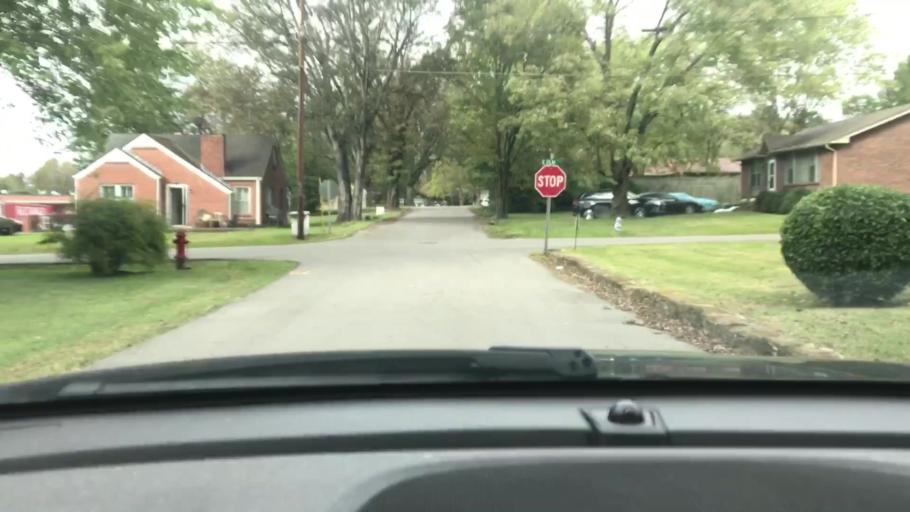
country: US
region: Tennessee
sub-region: Cheatham County
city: Ashland City
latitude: 36.2656
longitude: -87.0579
